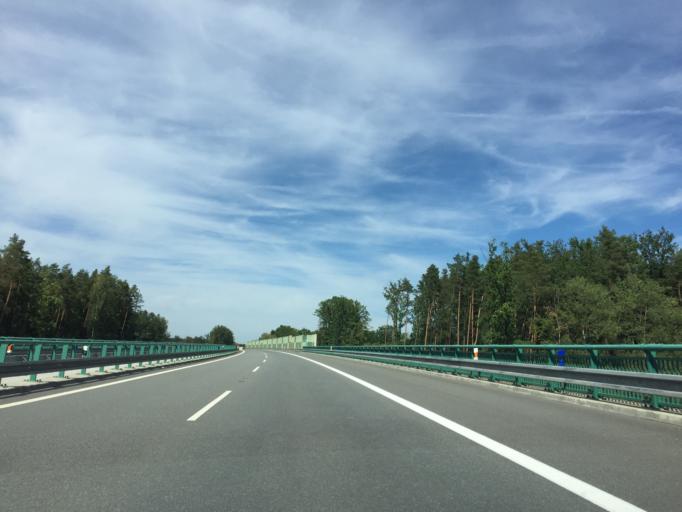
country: CZ
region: Jihocesky
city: Plana nad Luznici
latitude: 49.3815
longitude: 14.7254
